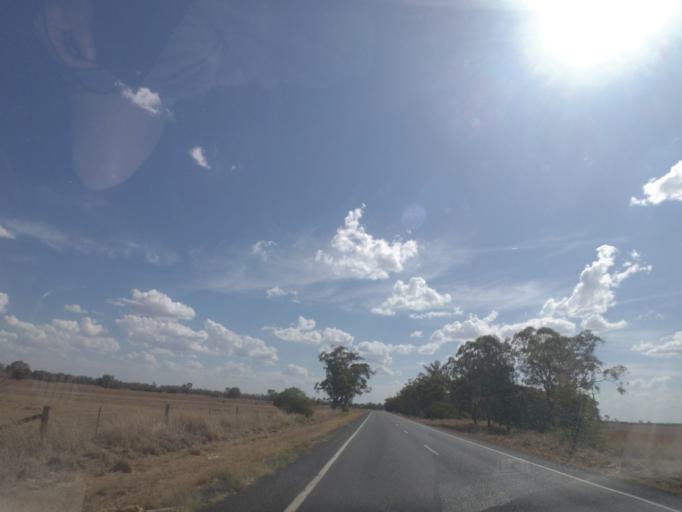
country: AU
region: Queensland
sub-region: Southern Downs
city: Stanthorpe
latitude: -28.4097
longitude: 151.1703
